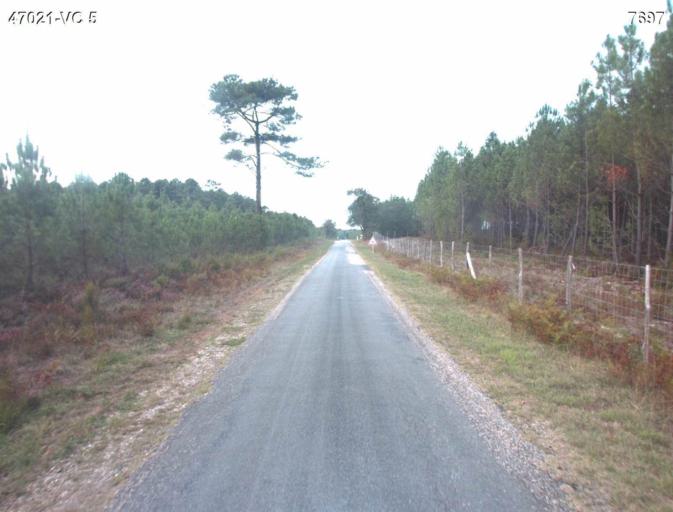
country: FR
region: Aquitaine
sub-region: Departement du Lot-et-Garonne
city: Barbaste
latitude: 44.1524
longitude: 0.2056
